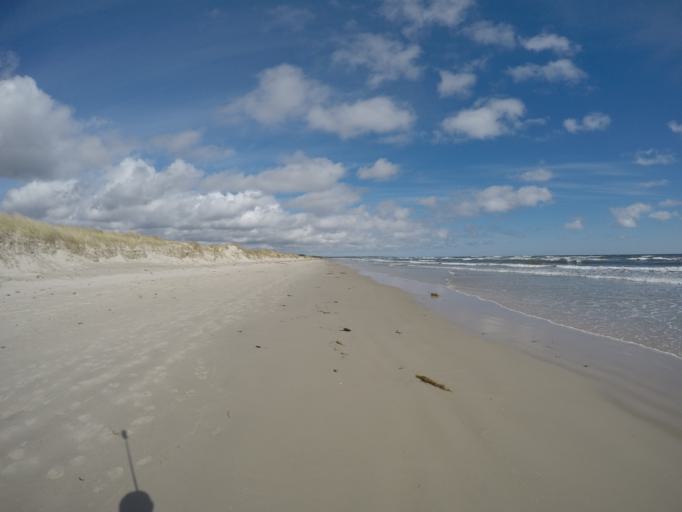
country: SE
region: Skane
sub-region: Simrishamns Kommun
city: Simrishamn
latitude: 55.4029
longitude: 14.2165
